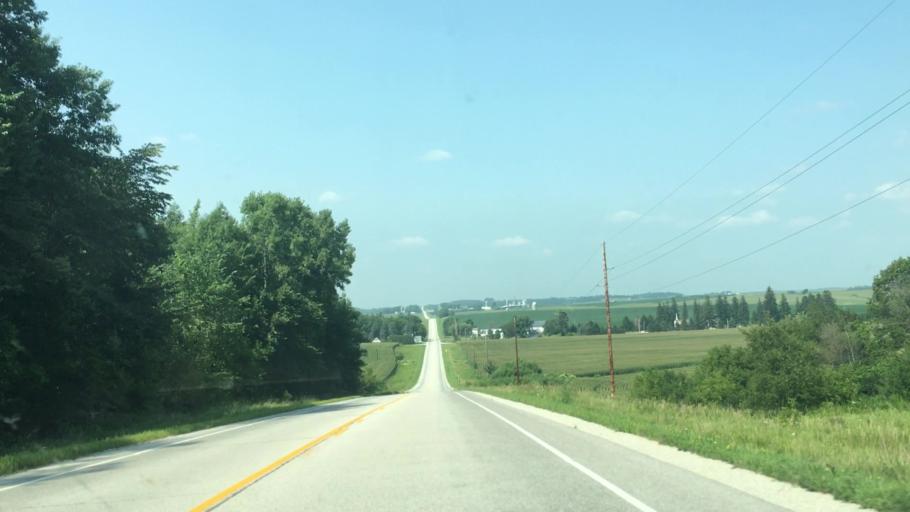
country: US
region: Minnesota
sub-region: Fillmore County
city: Harmony
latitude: 43.5879
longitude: -91.9298
